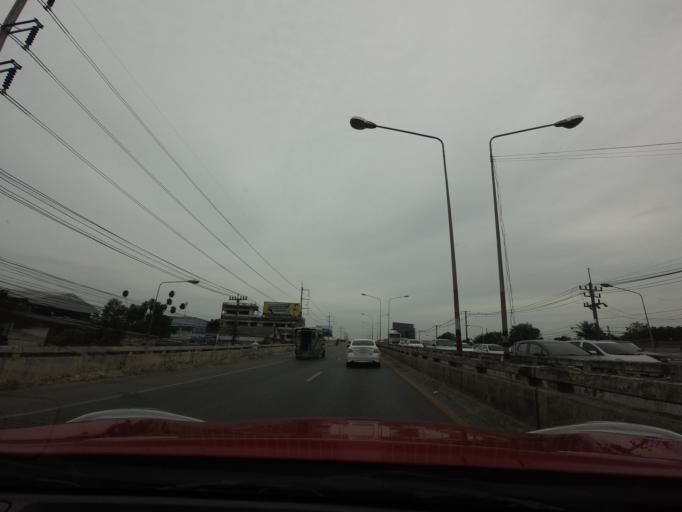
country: TH
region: Songkhla
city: Hat Yai
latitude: 6.9893
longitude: 100.4819
